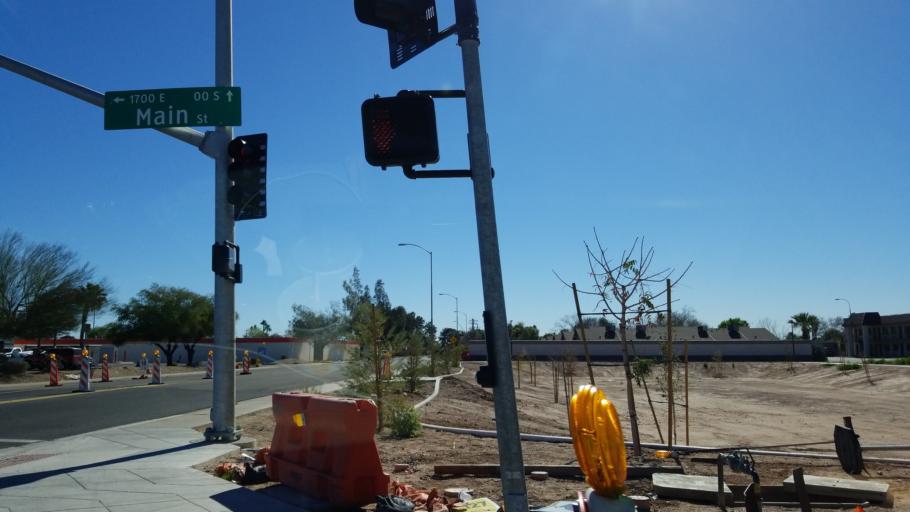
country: US
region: Arizona
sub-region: Maricopa County
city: Mesa
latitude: 33.4152
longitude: -111.7946
